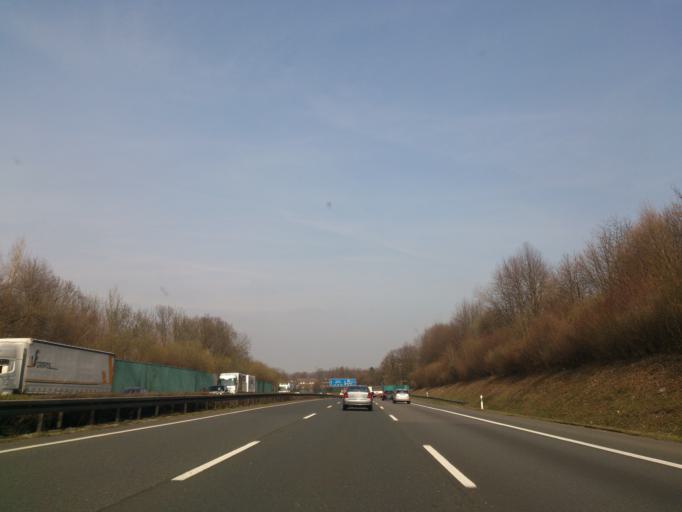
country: DE
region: North Rhine-Westphalia
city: Herdecke
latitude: 51.3773
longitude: 7.4287
